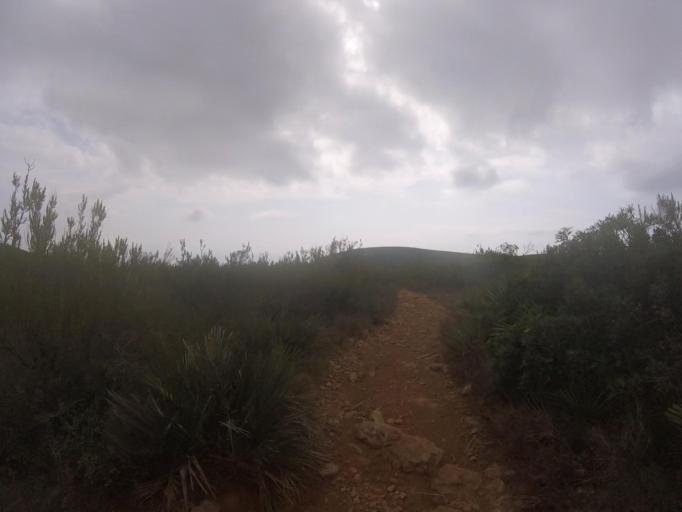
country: ES
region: Valencia
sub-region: Provincia de Castello
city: Santa Magdalena de Pulpis
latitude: 40.3482
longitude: 0.3439
